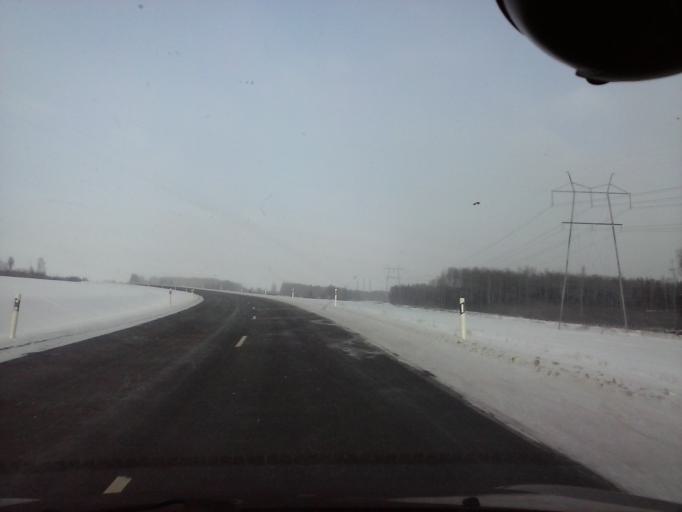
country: EE
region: Viljandimaa
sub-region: Abja vald
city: Abja-Paluoja
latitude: 58.2906
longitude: 25.2953
